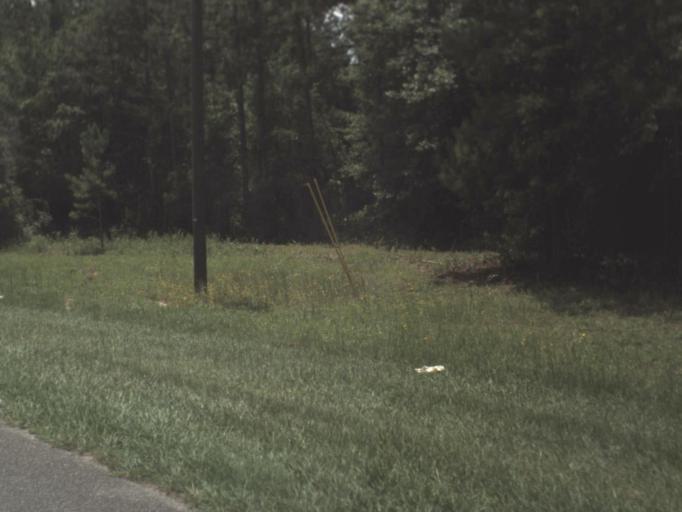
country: US
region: Florida
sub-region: Madison County
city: Madison
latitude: 30.4600
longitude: -83.3612
